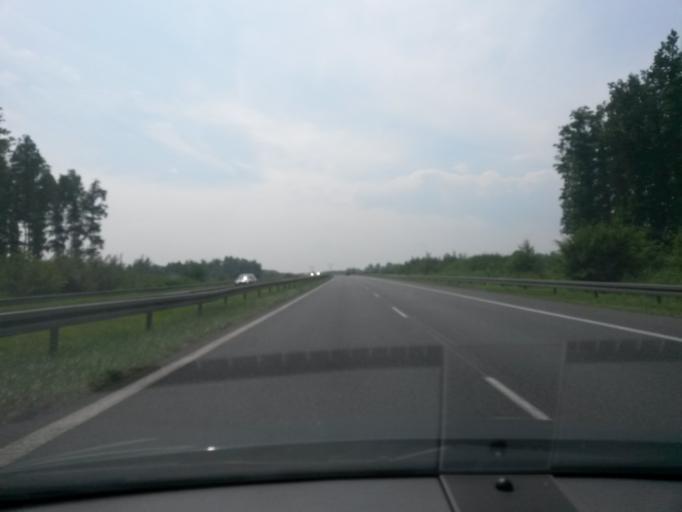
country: PL
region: Lodz Voivodeship
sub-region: Powiat piotrkowski
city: Wola Krzysztoporska
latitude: 51.3020
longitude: 19.5550
